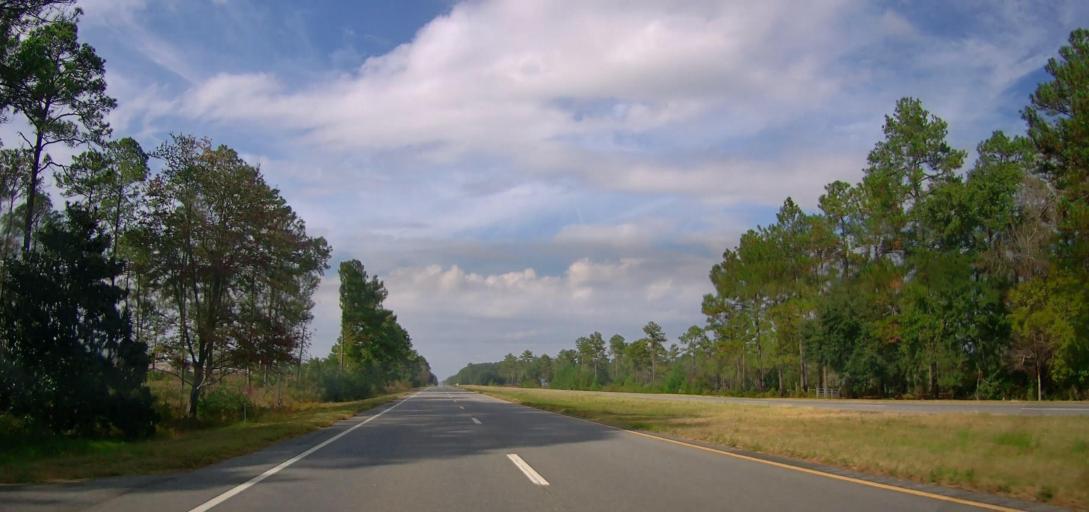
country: US
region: Georgia
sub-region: Thomas County
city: Meigs
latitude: 30.9579
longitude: -84.0282
